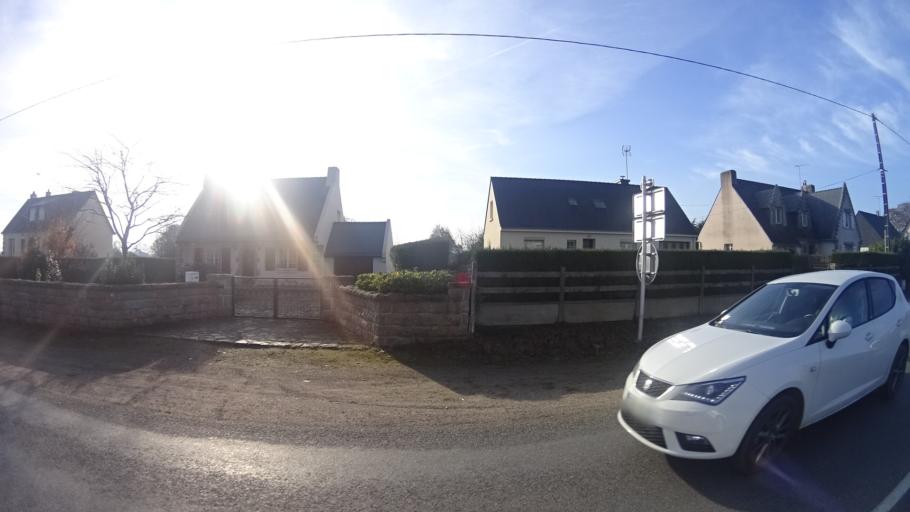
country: FR
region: Brittany
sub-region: Departement du Morbihan
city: Allaire
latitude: 47.6353
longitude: -2.1558
